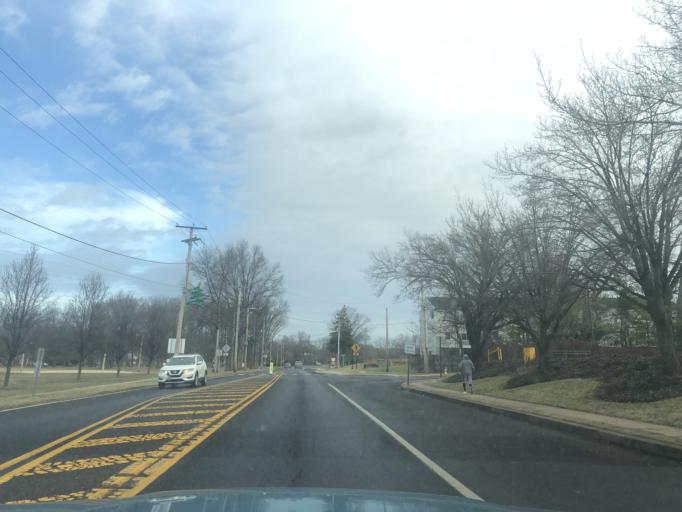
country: US
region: Pennsylvania
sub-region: Bucks County
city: Perkasie
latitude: 40.3643
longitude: -75.2983
